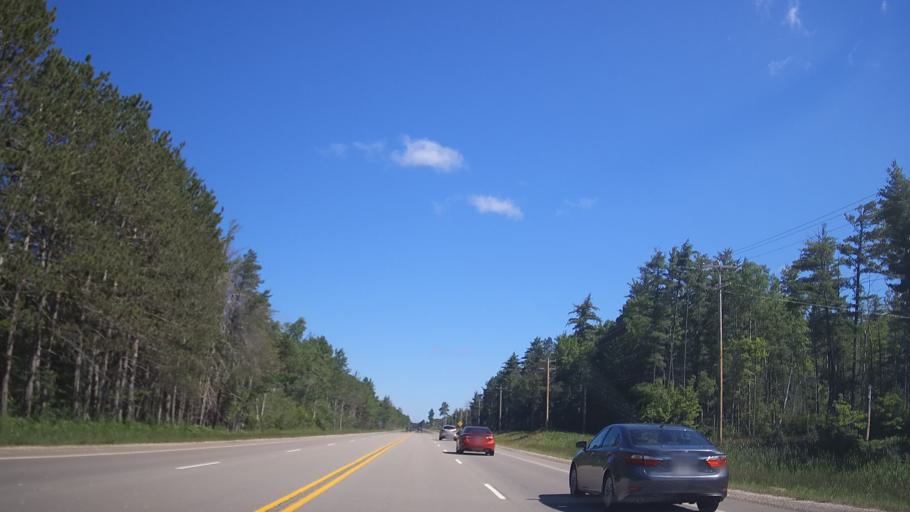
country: US
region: Michigan
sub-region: Cheboygan County
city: Indian River
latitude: 45.5186
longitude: -84.7816
